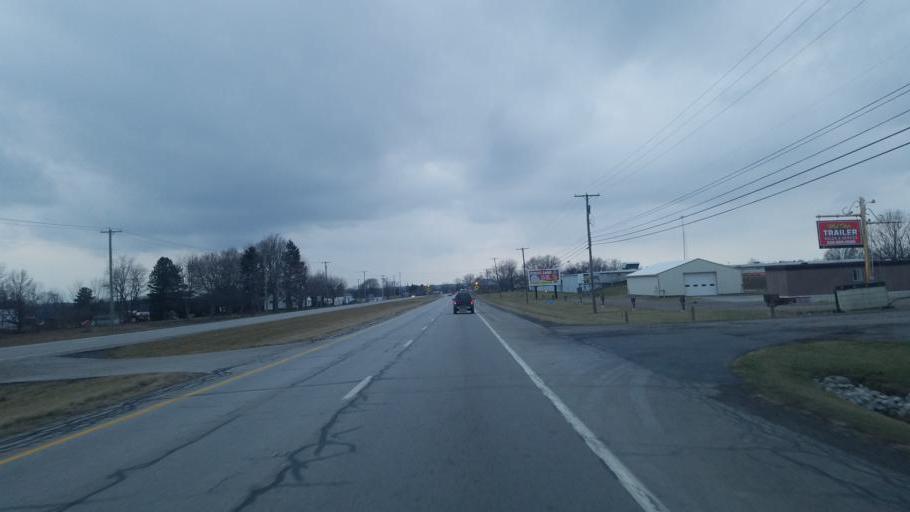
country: US
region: Ohio
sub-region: Wayne County
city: Dalton
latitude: 40.8006
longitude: -81.7203
